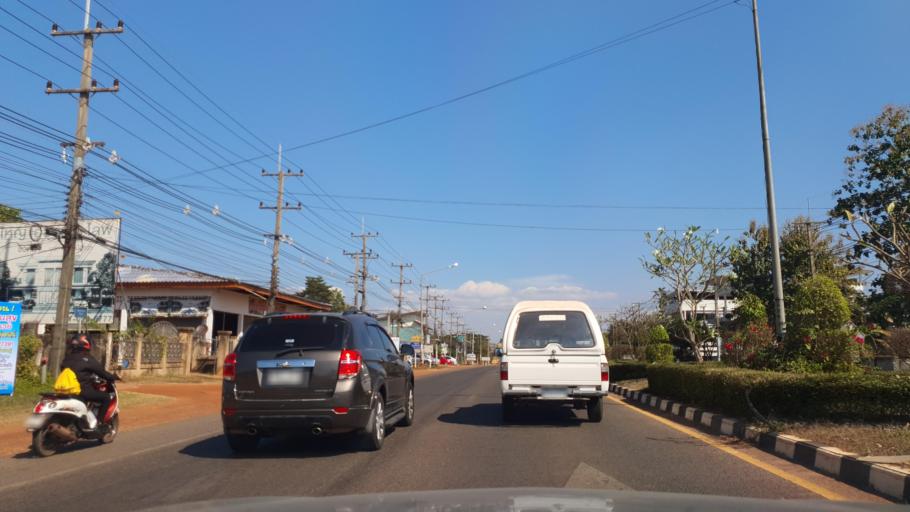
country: TH
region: Sakon Nakhon
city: Sakon Nakhon
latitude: 17.1425
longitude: 104.1125
